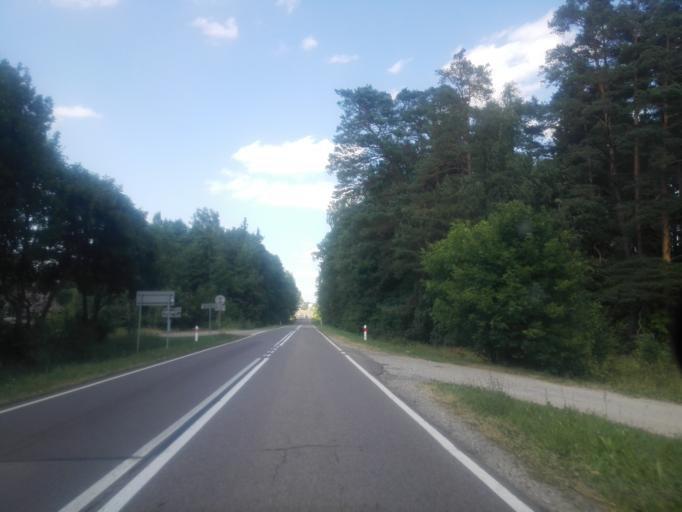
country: PL
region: Podlasie
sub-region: Powiat sejnenski
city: Sejny
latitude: 54.0331
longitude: 23.3531
